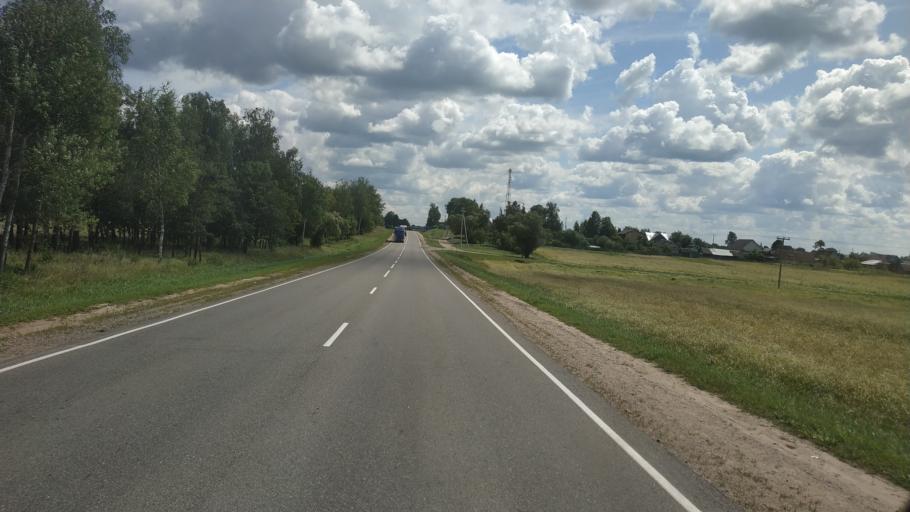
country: BY
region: Mogilev
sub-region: Mahilyowski Rayon
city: Veyno
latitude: 53.8169
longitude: 30.4451
